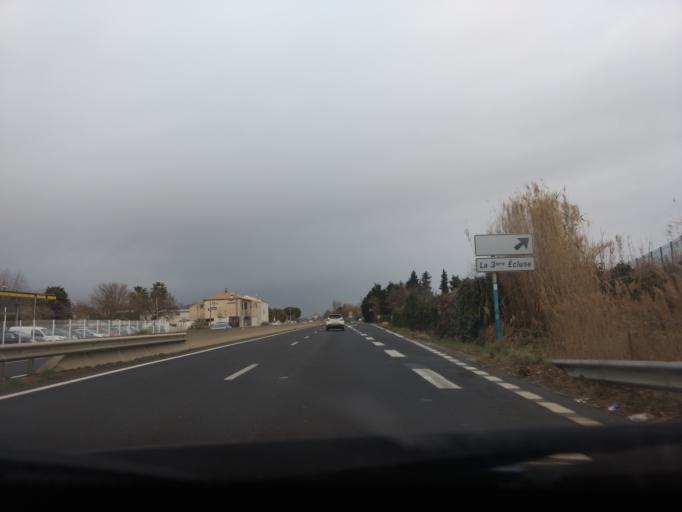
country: FR
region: Languedoc-Roussillon
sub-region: Departement de l'Herault
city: Lattes
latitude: 43.5591
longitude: 3.8933
